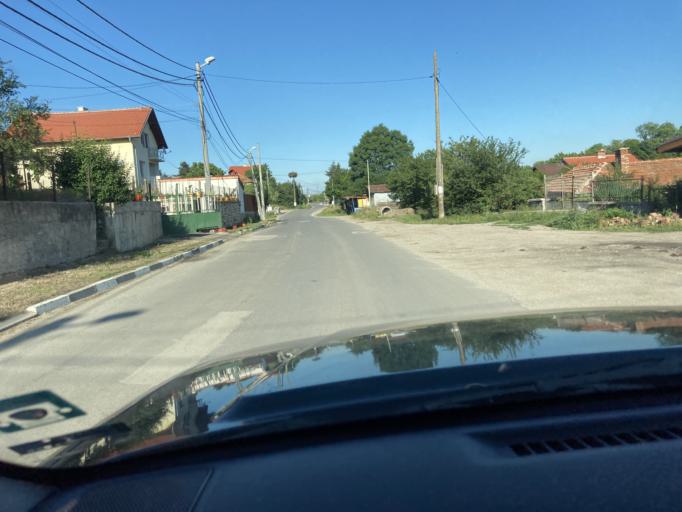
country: BG
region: Sofiya
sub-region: Obshtina Slivnitsa
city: Slivnitsa
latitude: 42.8454
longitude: 22.9990
